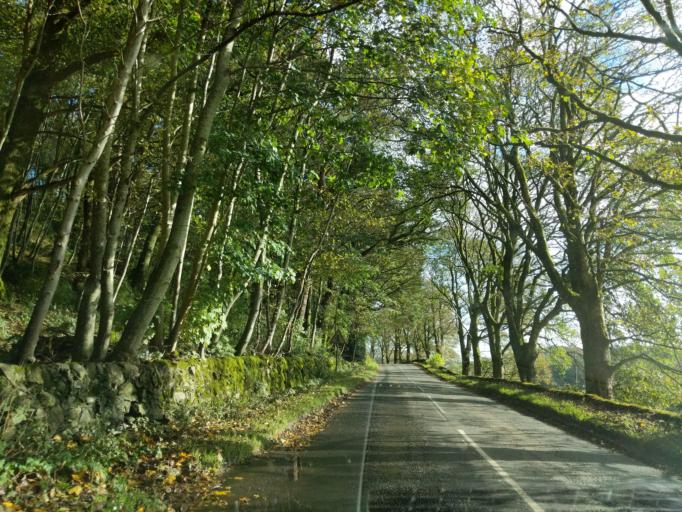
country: GB
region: Scotland
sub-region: Dumfries and Galloway
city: Thornhill
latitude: 55.1934
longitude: -3.8970
